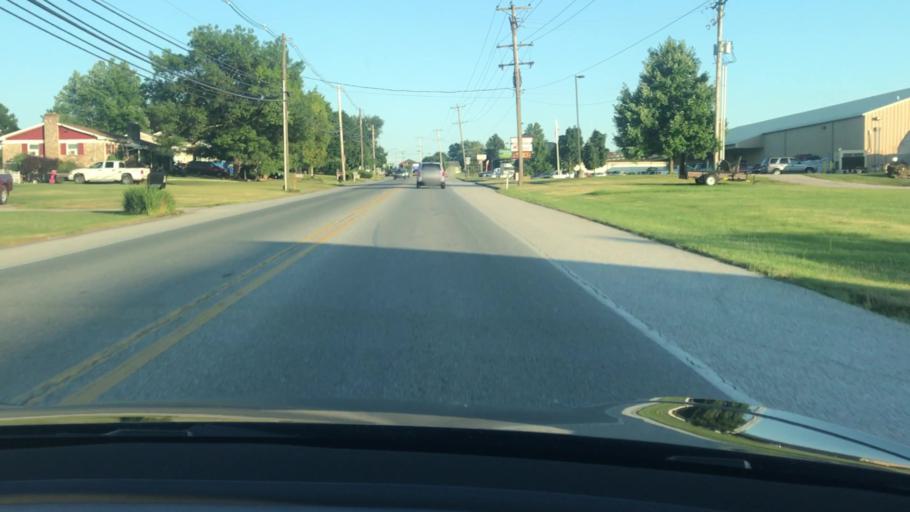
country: US
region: Pennsylvania
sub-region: York County
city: Dover
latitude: 39.9963
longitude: -76.8449
